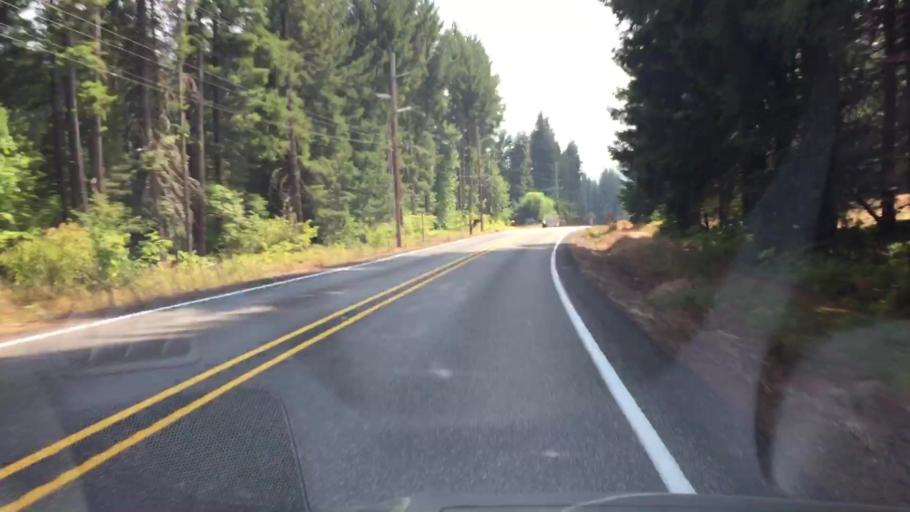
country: US
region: Washington
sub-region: Klickitat County
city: White Salmon
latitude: 45.8649
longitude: -121.5107
